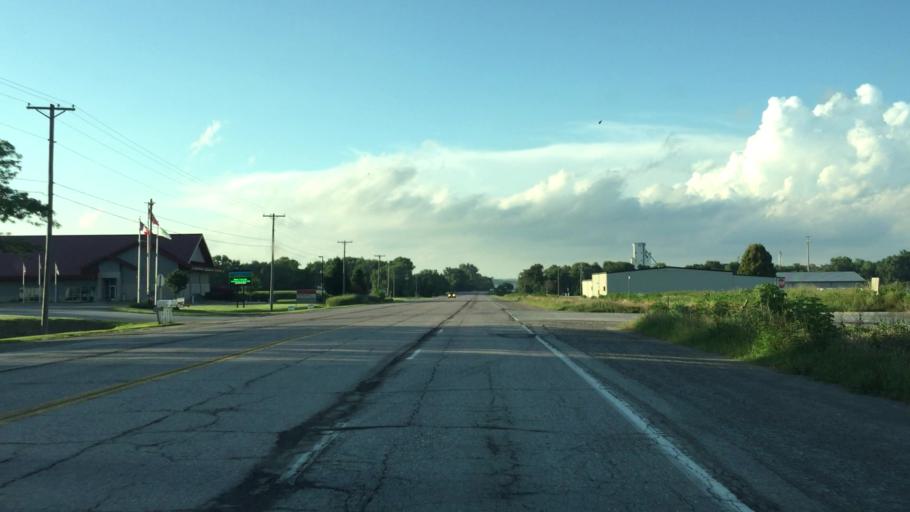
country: US
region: Iowa
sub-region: Johnson County
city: University Heights
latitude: 41.6222
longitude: -91.5446
